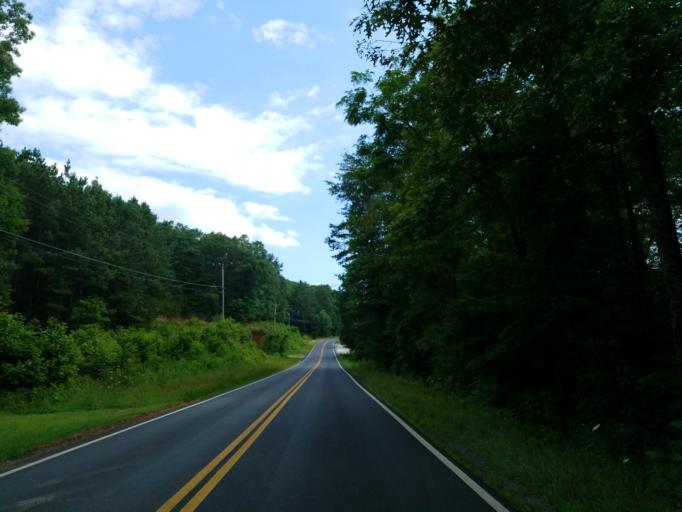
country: US
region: Georgia
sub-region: Fannin County
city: Blue Ridge
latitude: 34.8535
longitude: -84.3016
